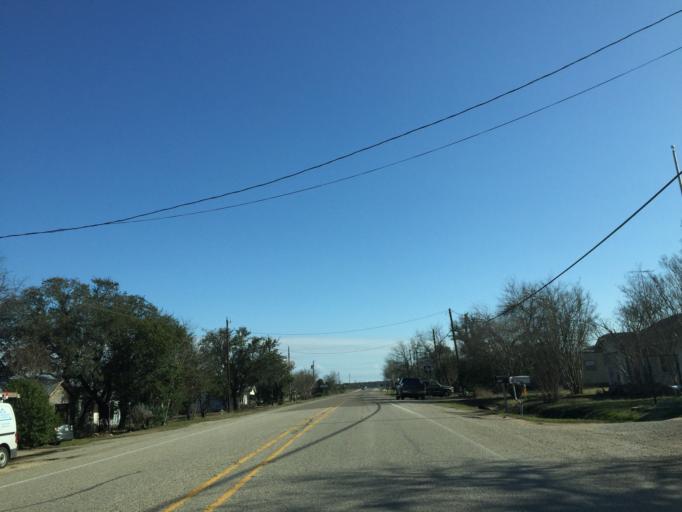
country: US
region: Texas
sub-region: Williamson County
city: Florence
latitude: 30.7822
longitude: -97.8525
